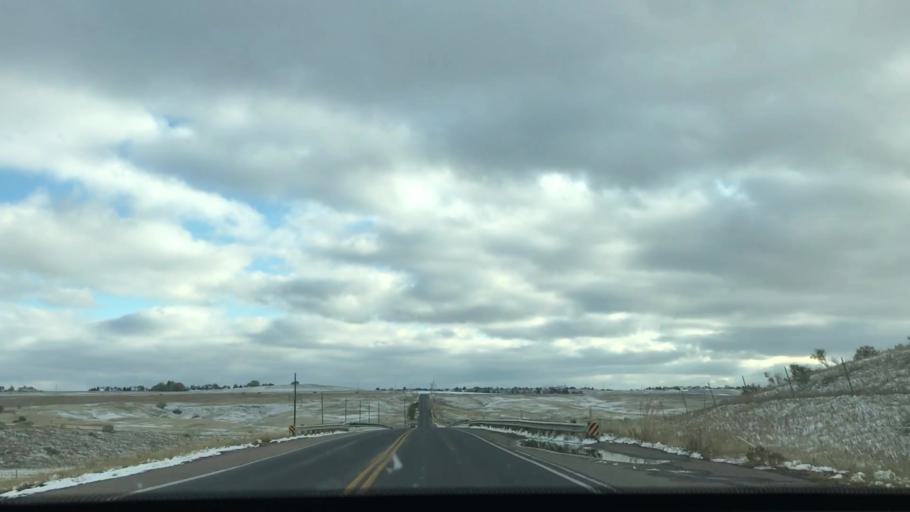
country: US
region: Colorado
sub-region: Boulder County
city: Lafayette
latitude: 39.9689
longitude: -105.0719
